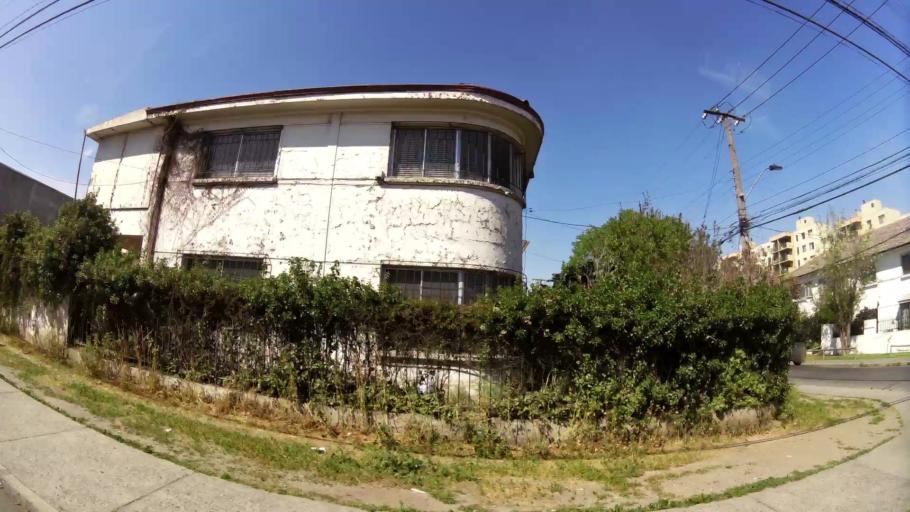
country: CL
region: Santiago Metropolitan
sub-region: Provincia de Santiago
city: Santiago
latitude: -33.5114
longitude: -70.6549
